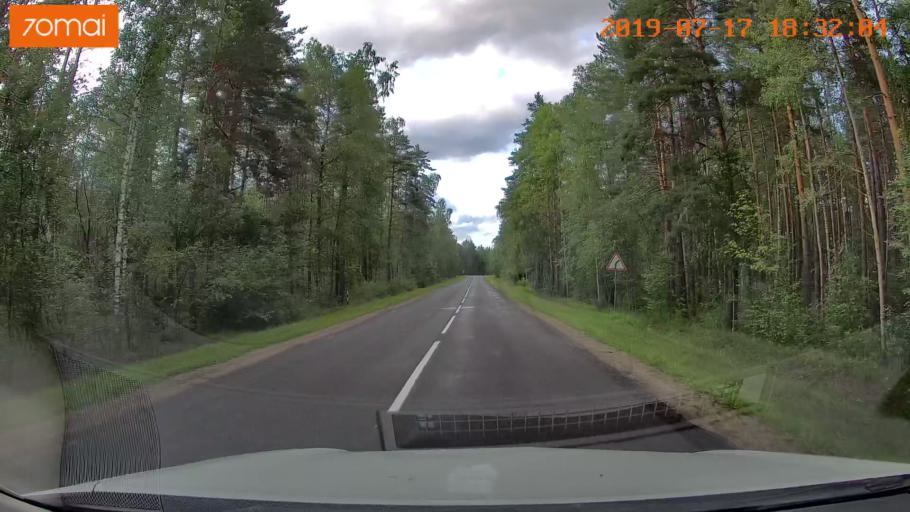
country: BY
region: Mogilev
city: Asipovichy
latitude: 53.2664
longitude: 28.6774
